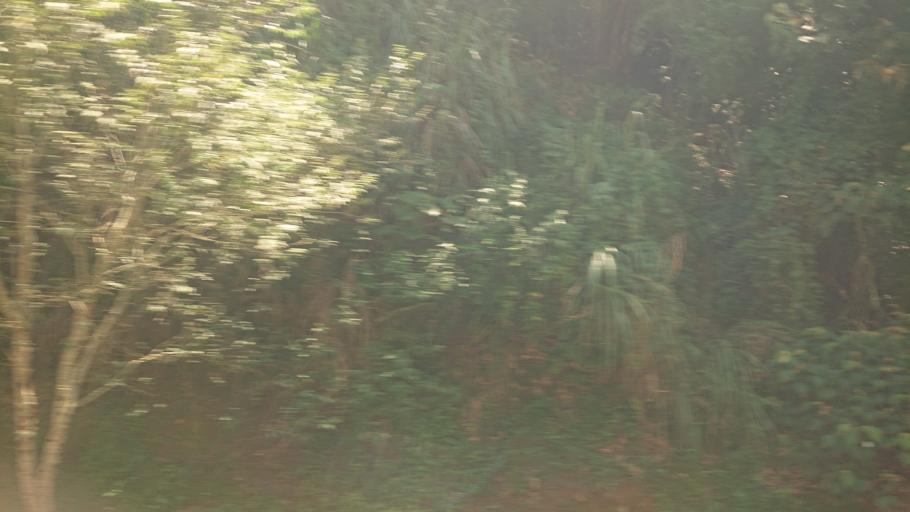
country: TW
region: Taiwan
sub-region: Nantou
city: Puli
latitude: 24.0540
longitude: 120.9339
